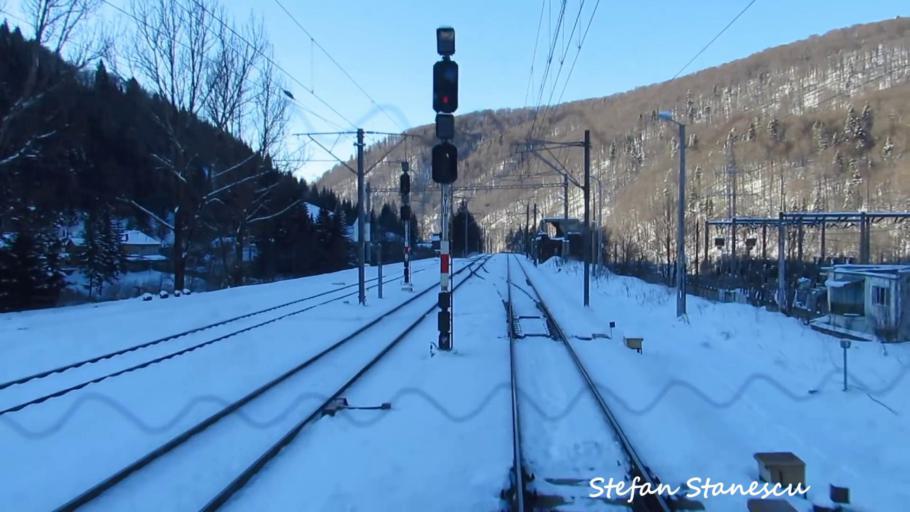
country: RO
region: Prahova
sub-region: Oras Azuga
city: Azuga
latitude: 45.4357
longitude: 25.5509
